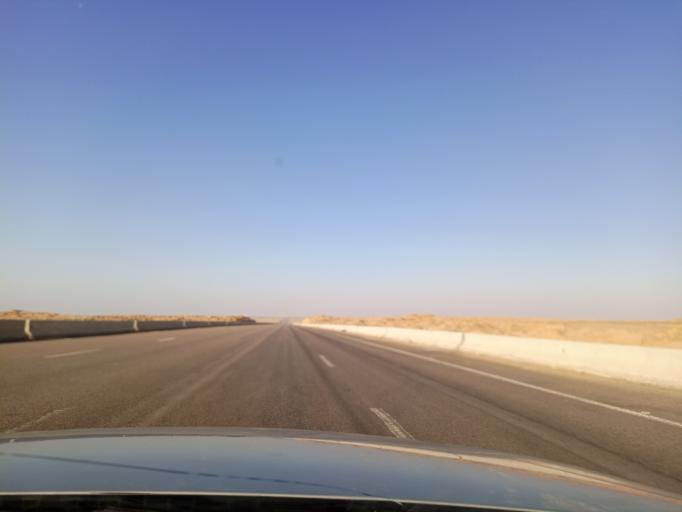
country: EG
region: Muhafazat al Fayyum
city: Tamiyah
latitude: 29.6174
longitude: 30.9375
